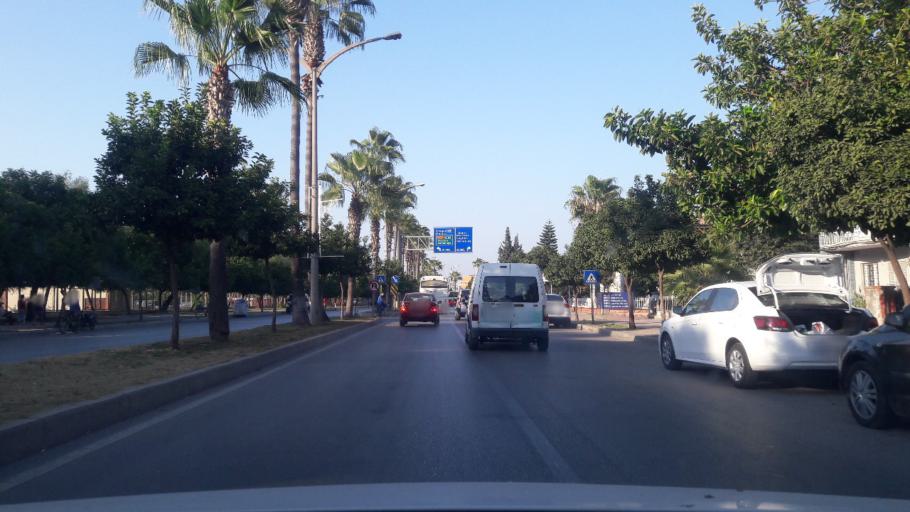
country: TR
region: Adana
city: Seyhan
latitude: 36.9906
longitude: 35.2986
